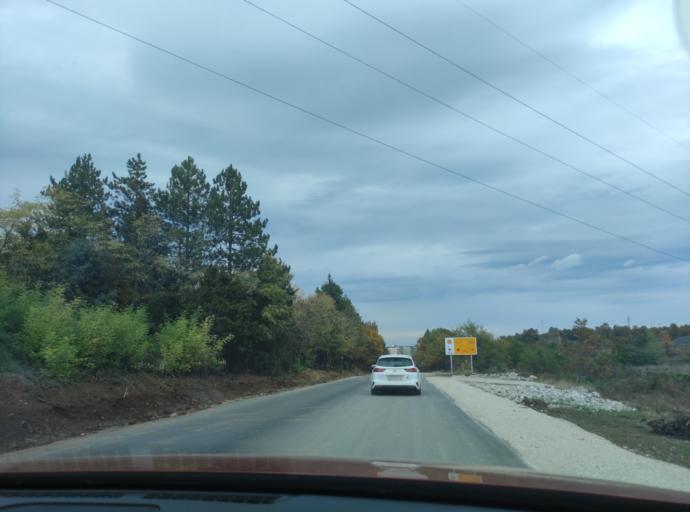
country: BG
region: Montana
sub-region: Obshtina Montana
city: Montana
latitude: 43.3913
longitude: 23.2417
